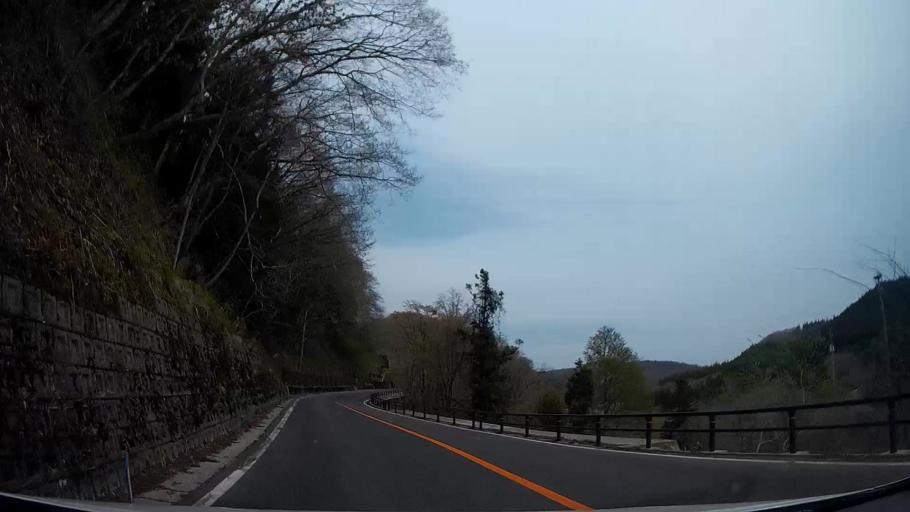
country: JP
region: Akita
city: Hanawa
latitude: 40.3761
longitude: 140.8889
